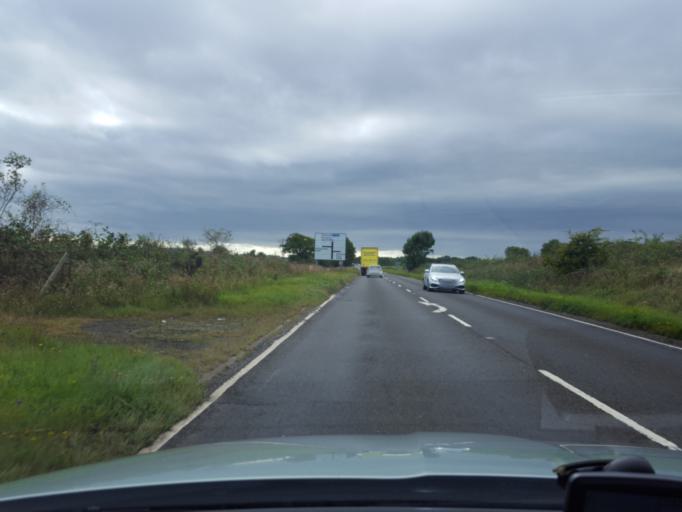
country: GB
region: Scotland
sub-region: Perth and Kinross
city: Milnathort
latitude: 56.2475
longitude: -3.3693
